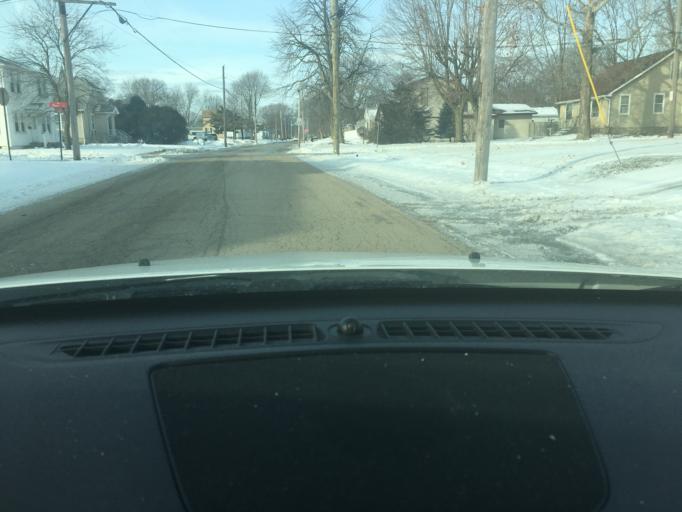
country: US
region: Illinois
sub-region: LaSalle County
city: Peru
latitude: 41.3304
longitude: -89.1235
